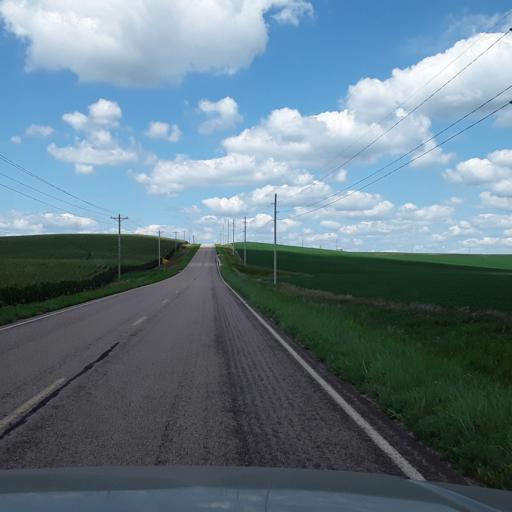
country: US
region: Nebraska
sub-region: Nance County
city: Genoa
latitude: 41.5470
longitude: -97.6961
